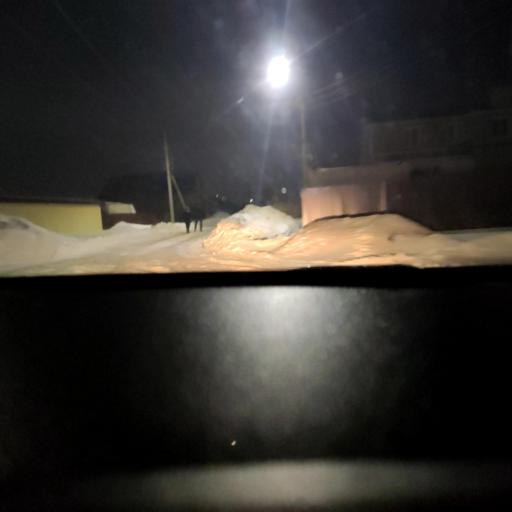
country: RU
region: Tatarstan
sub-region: Chistopol'skiy Rayon
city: Chistopol'
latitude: 55.3574
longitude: 50.6704
